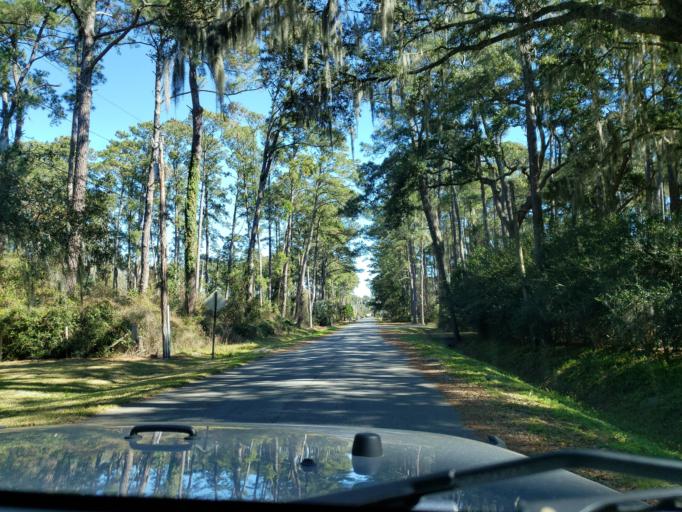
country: US
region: Georgia
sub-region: Chatham County
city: Wilmington Island
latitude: 32.0378
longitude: -80.9766
